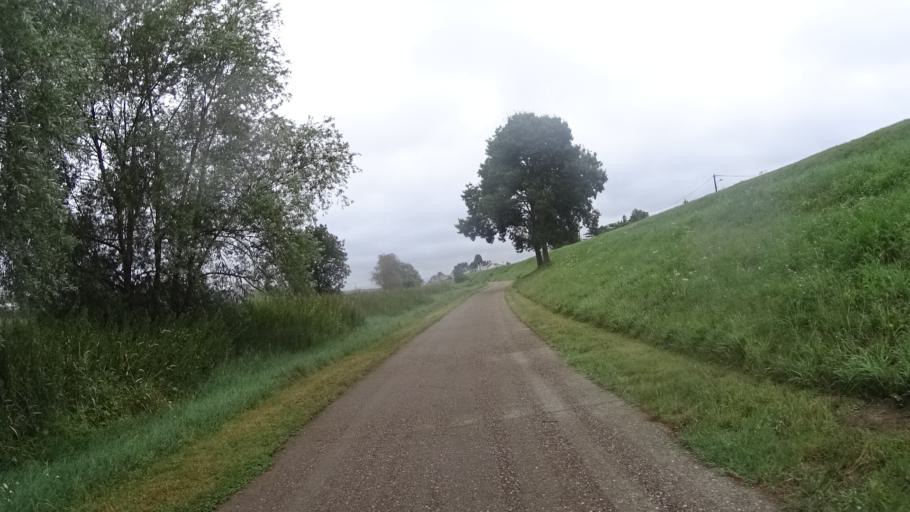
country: FR
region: Centre
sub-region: Departement du Loir-et-Cher
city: Blois
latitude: 47.5762
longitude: 1.3266
